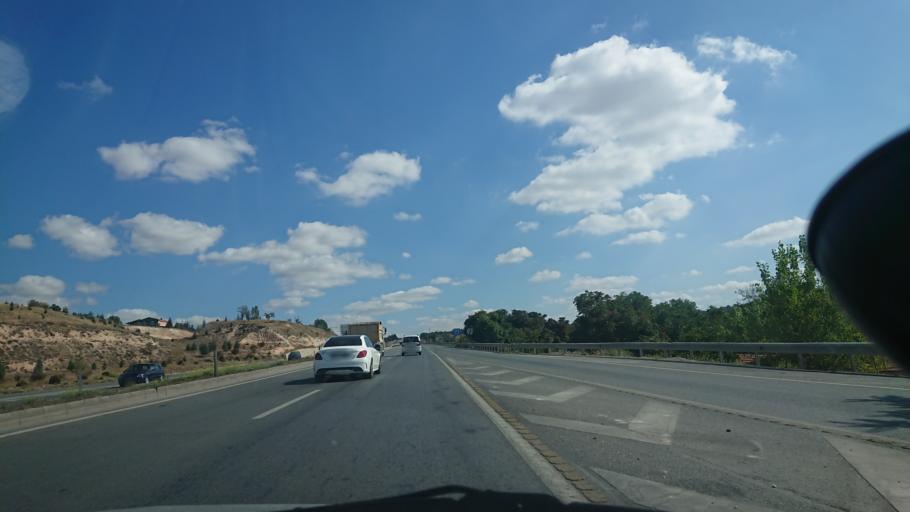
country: TR
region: Eskisehir
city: Sevinc
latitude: 39.7278
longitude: 30.6634
